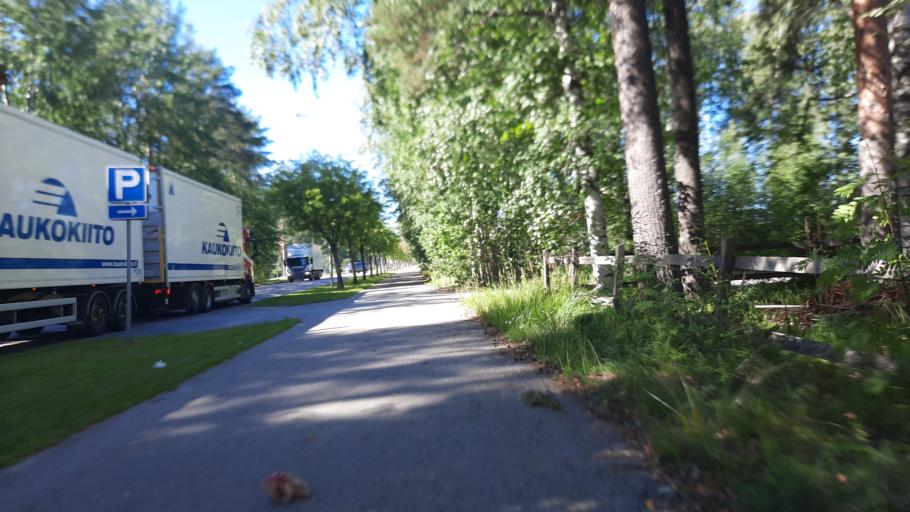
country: FI
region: North Karelia
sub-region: Joensuu
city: Joensuu
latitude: 62.6208
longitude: 29.7631
